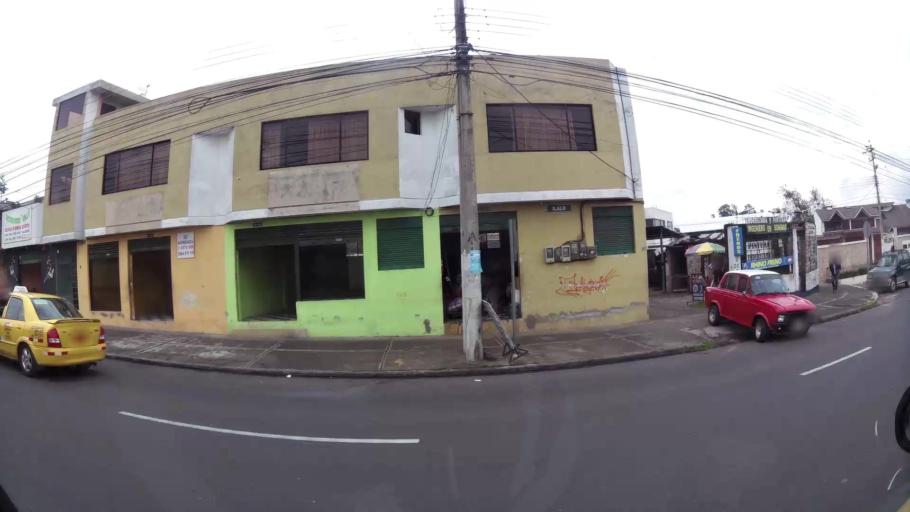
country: EC
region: Pichincha
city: Sangolqui
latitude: -0.3053
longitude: -78.4685
